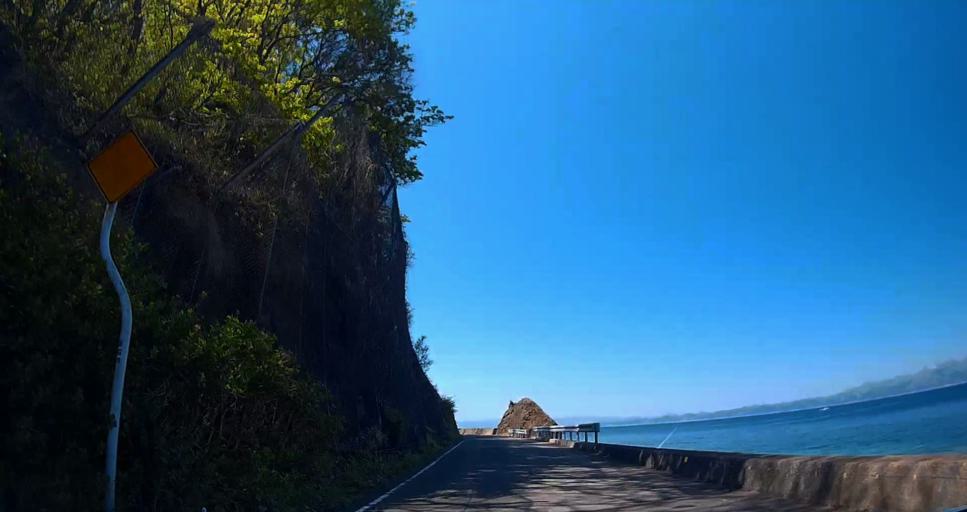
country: JP
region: Aomori
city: Aomori Shi
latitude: 41.1371
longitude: 140.7783
